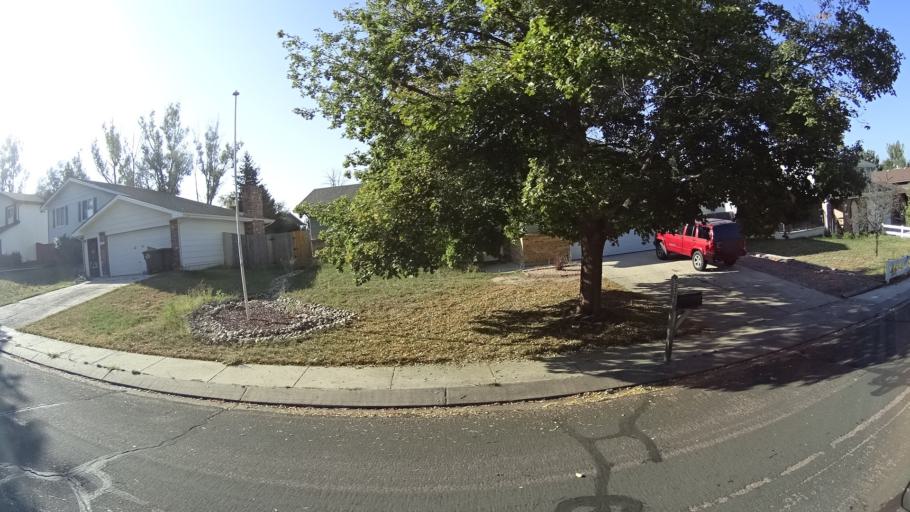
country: US
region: Colorado
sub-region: El Paso County
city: Cimarron Hills
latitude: 38.8885
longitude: -104.7289
